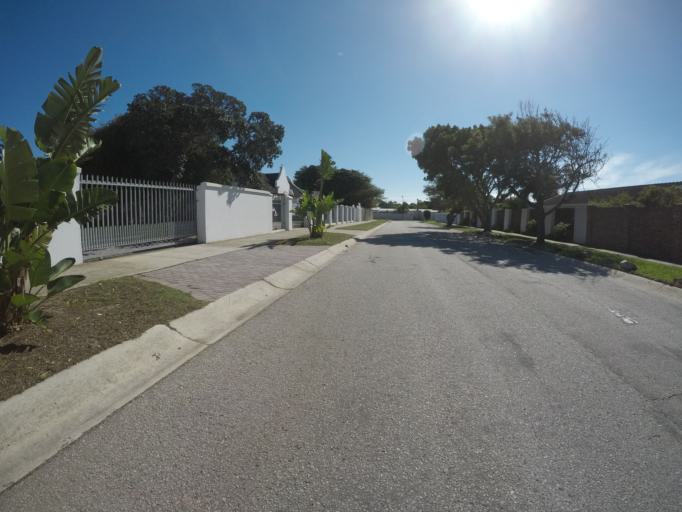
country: ZA
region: Eastern Cape
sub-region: Nelson Mandela Bay Metropolitan Municipality
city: Port Elizabeth
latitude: -33.9960
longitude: 25.6677
